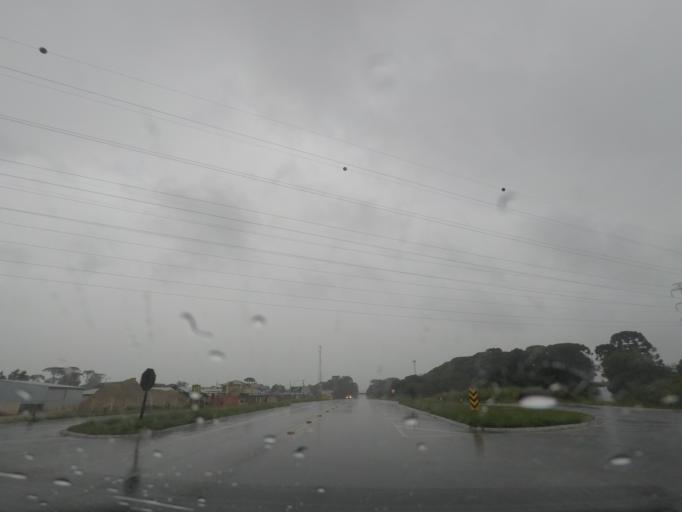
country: BR
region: Parana
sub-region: Almirante Tamandare
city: Almirante Tamandare
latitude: -25.3536
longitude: -49.2988
